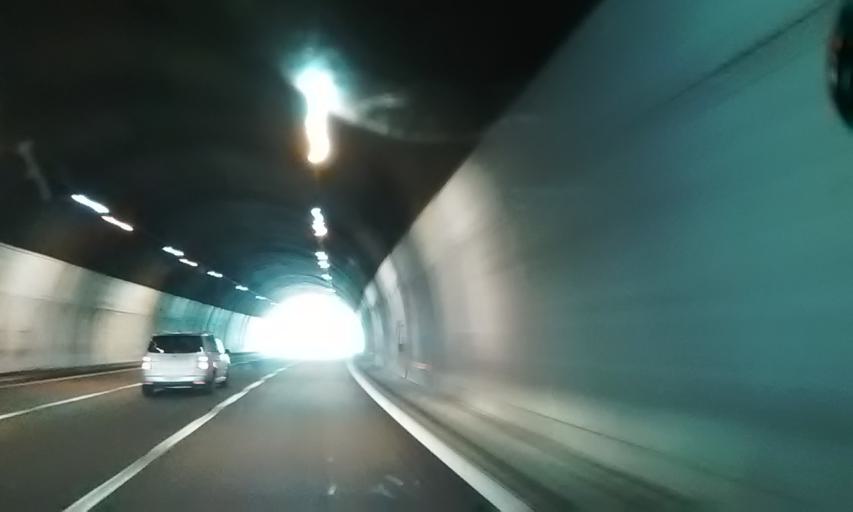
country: IT
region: Liguria
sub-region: Provincia di Genova
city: Rossiglione
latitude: 44.5654
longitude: 8.6631
